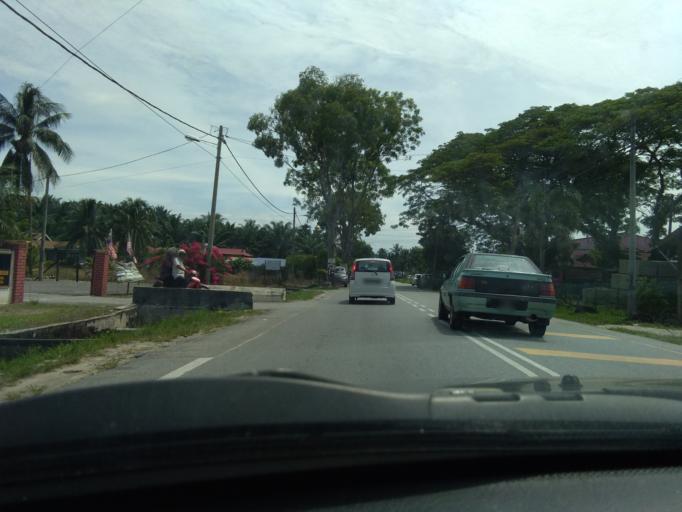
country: MY
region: Perak
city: Bagan Serai
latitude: 5.0511
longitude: 100.5873
